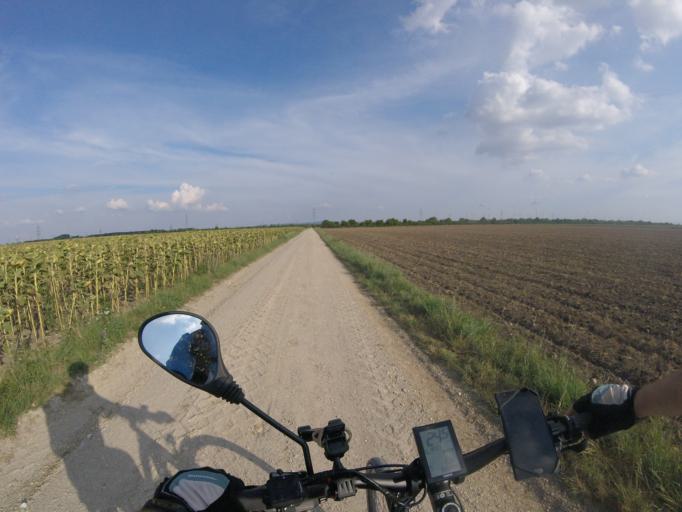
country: AT
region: Lower Austria
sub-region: Politischer Bezirk Baden
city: Trumau
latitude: 47.9801
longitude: 16.3578
